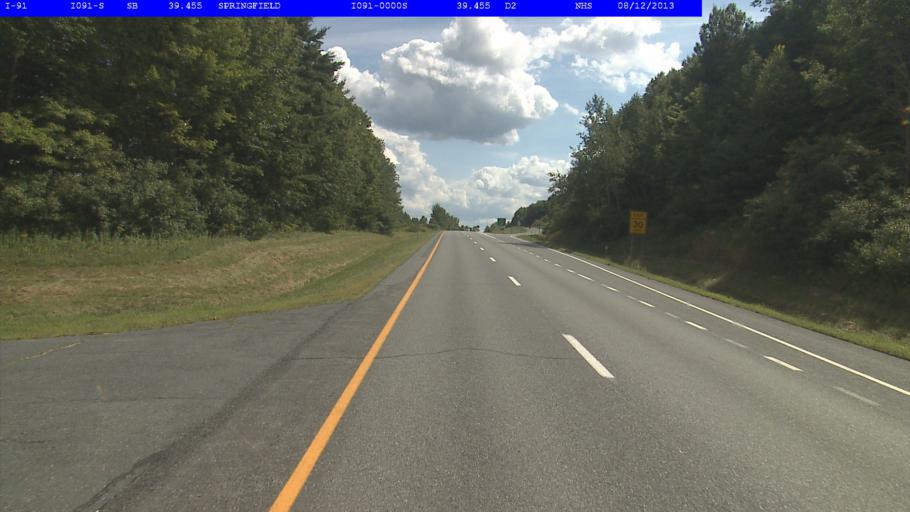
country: US
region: New Hampshire
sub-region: Sullivan County
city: Charlestown
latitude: 43.2379
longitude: -72.4481
